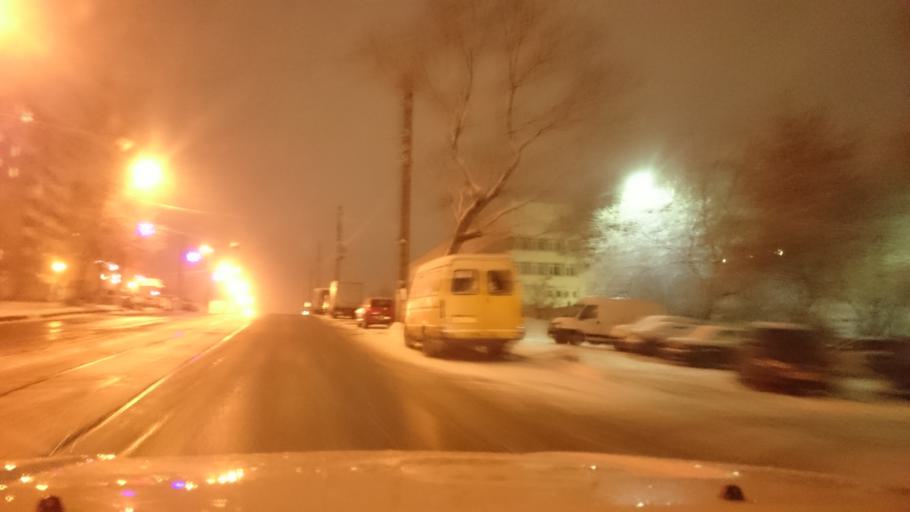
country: RU
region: Tula
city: Tula
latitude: 54.2142
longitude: 37.6151
